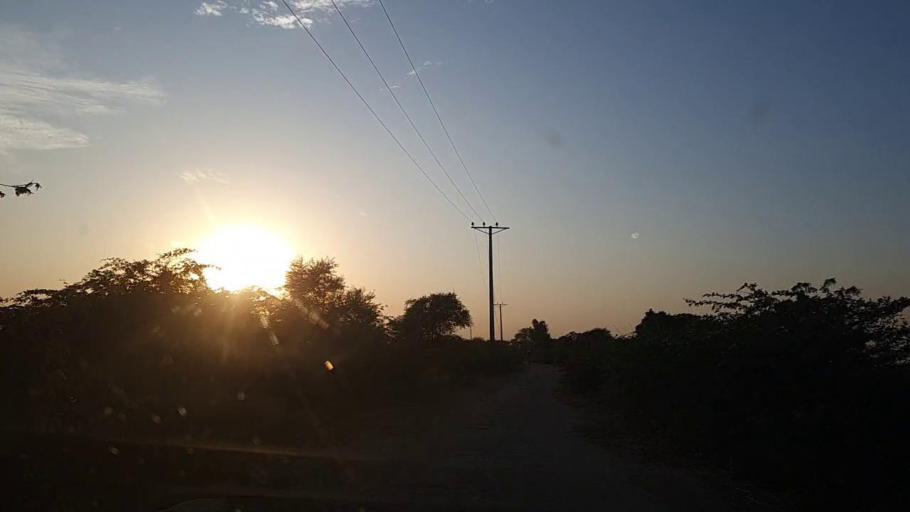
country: PK
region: Sindh
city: Thatta
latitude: 24.7982
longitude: 67.9459
